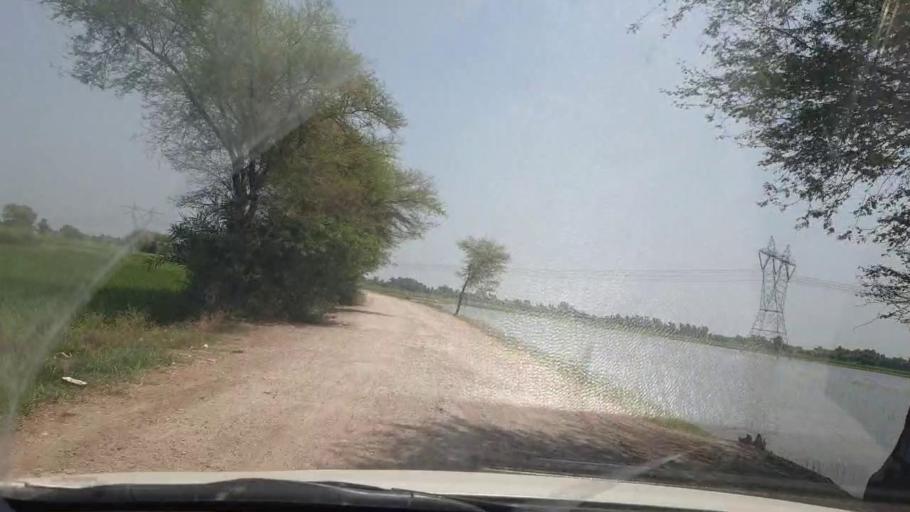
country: PK
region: Sindh
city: Shikarpur
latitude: 27.9172
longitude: 68.6861
